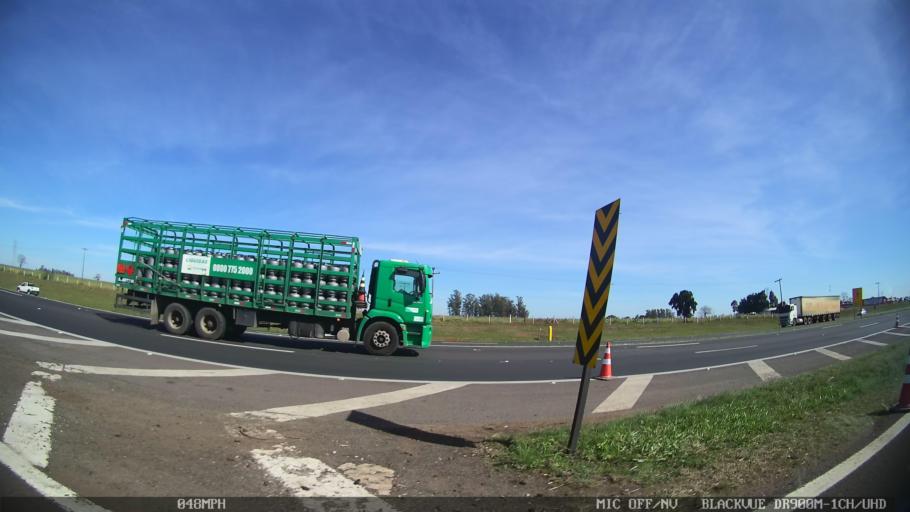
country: BR
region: Sao Paulo
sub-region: Pirassununga
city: Pirassununga
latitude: -22.0821
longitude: -47.4211
